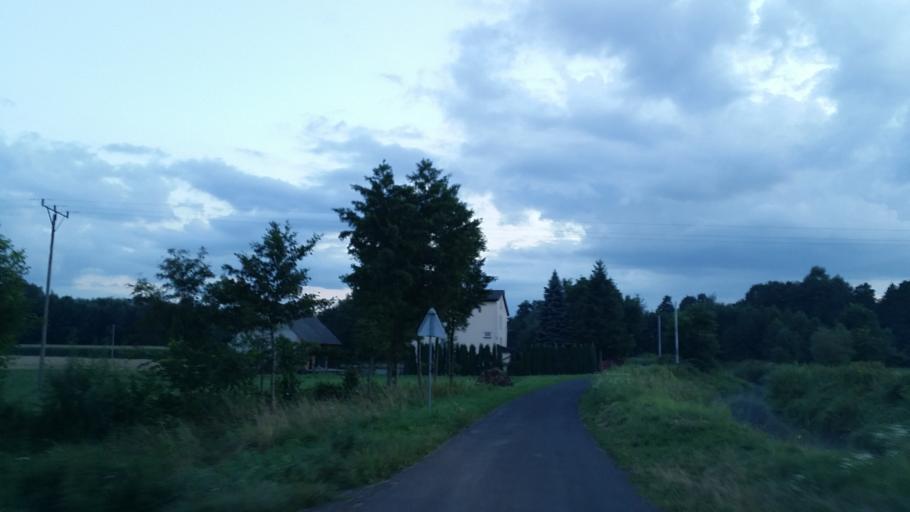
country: PL
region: Lesser Poland Voivodeship
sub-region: Powiat oswiecimski
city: Przeciszow
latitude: 50.0102
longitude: 19.3789
